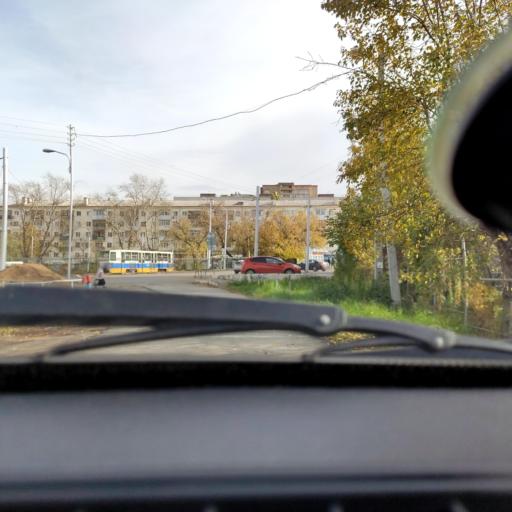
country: RU
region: Bashkortostan
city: Ufa
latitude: 54.7266
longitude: 55.9229
